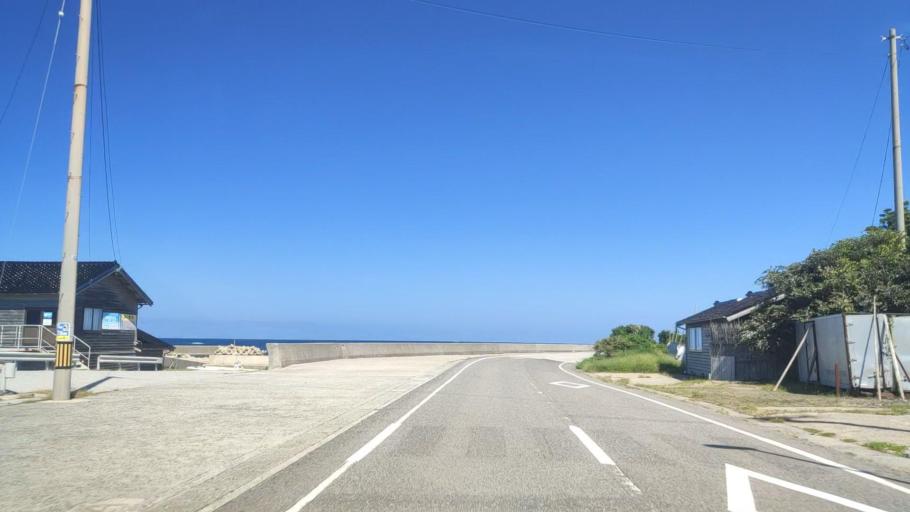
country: JP
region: Ishikawa
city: Nanao
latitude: 37.5290
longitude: 137.2879
